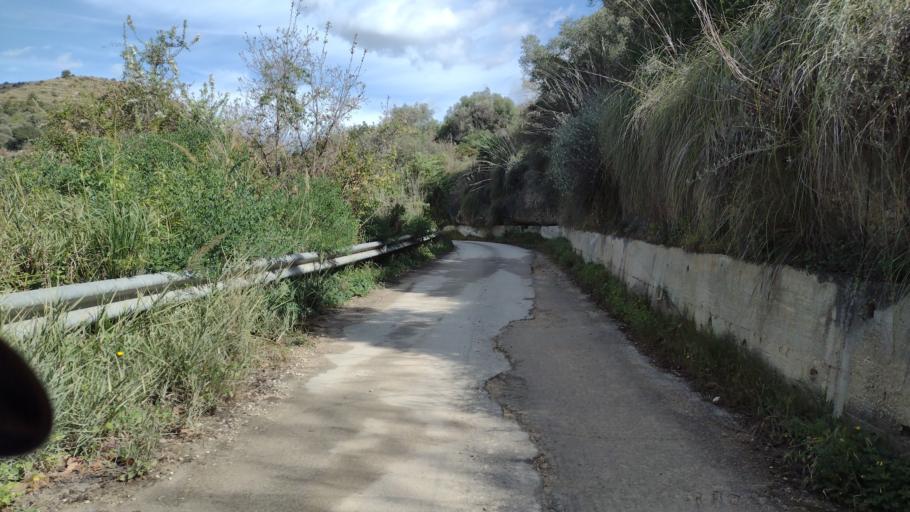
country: IT
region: Sicily
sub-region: Provincia di Siracusa
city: Noto
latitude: 36.9075
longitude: 15.0175
